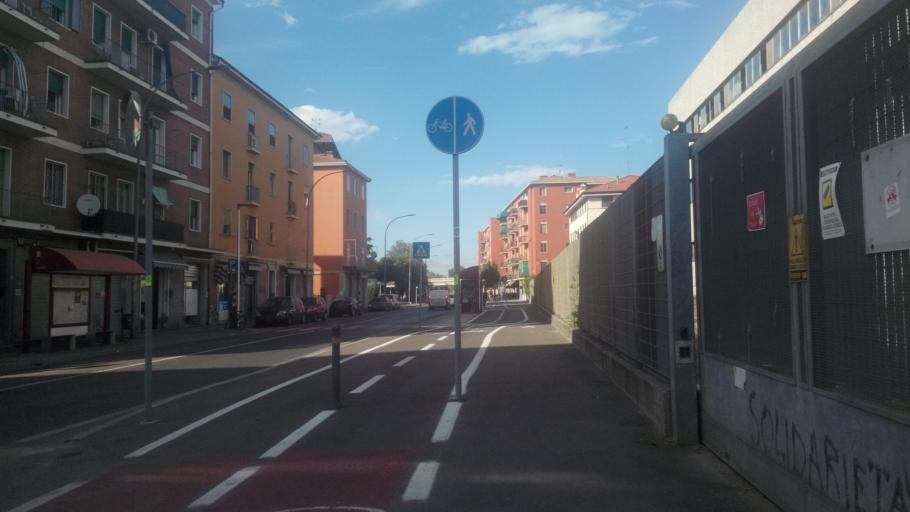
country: IT
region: Emilia-Romagna
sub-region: Provincia di Bologna
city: Bologna
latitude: 44.5176
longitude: 11.3557
